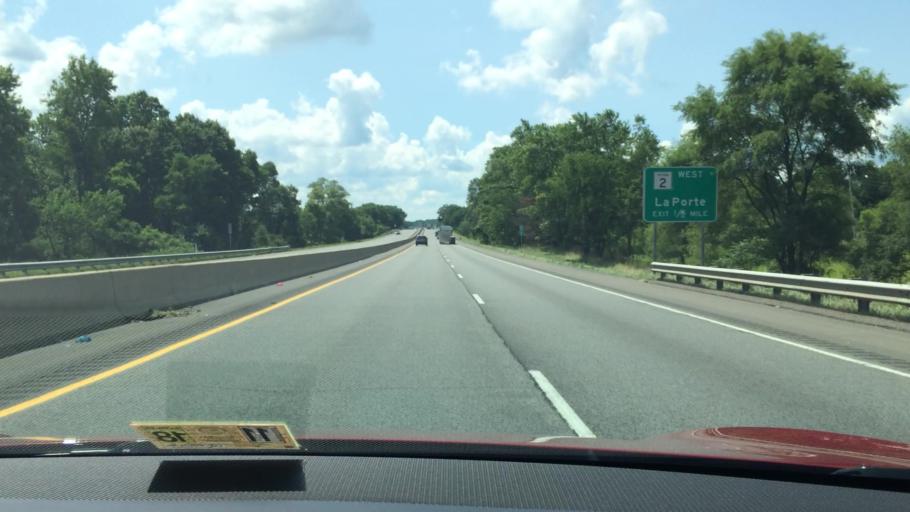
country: US
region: Indiana
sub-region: Saint Joseph County
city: South Bend
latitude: 41.6843
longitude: -86.3410
